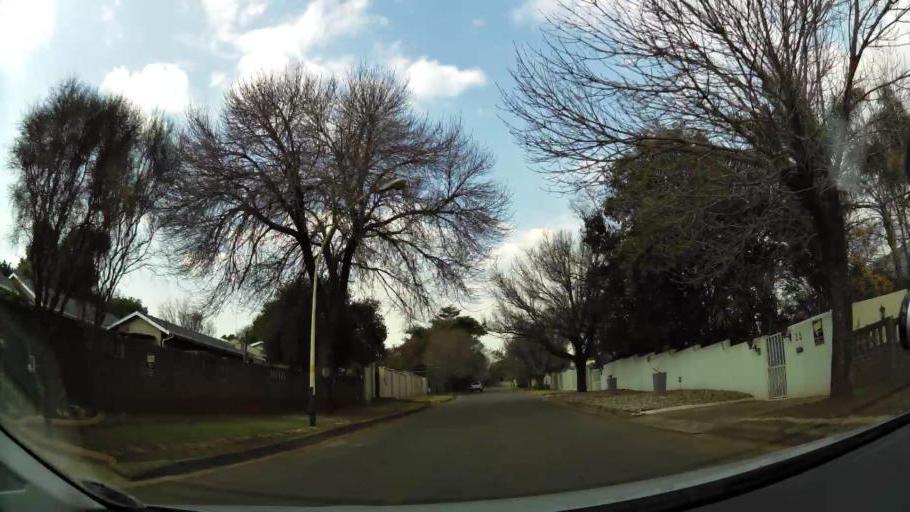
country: ZA
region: Gauteng
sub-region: City of Johannesburg Metropolitan Municipality
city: Modderfontein
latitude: -26.1391
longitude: 28.1890
